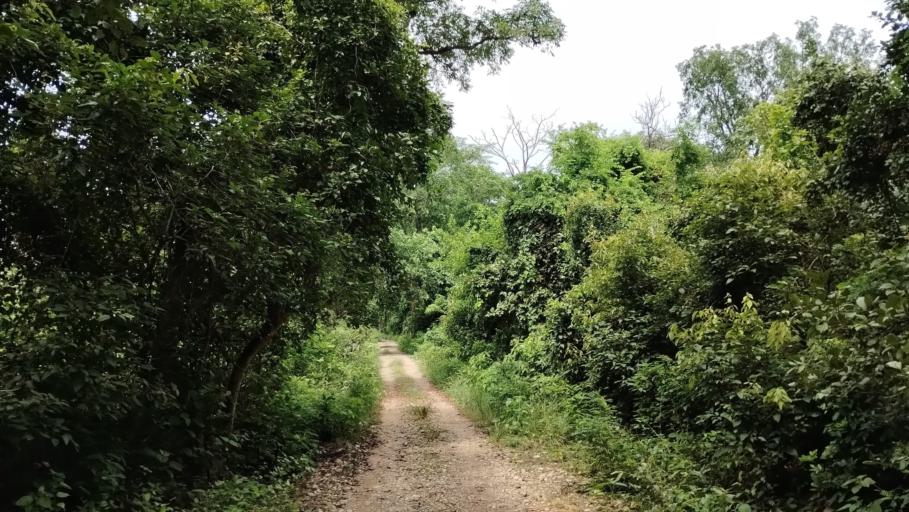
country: NP
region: Far Western
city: Tikapur
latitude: 28.4559
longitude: 81.2423
